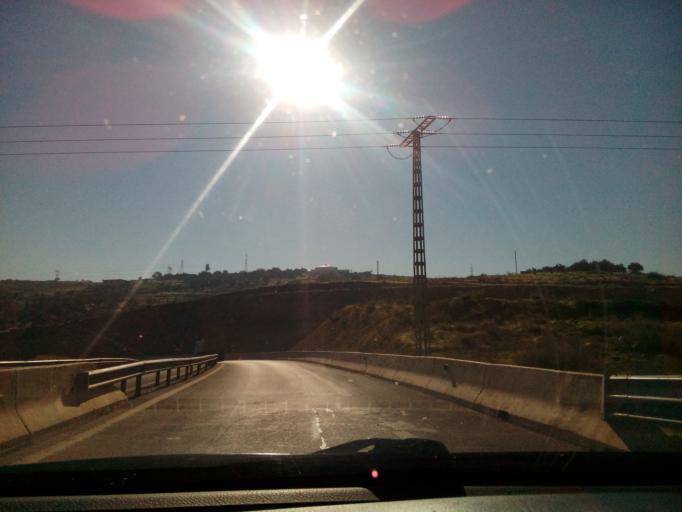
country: DZ
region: Chlef
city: Boukadir
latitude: 36.0541
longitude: 1.1368
